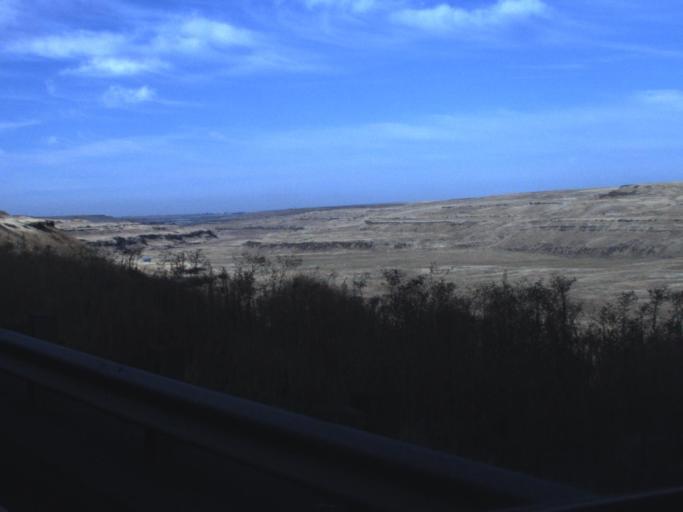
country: US
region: Washington
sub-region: Franklin County
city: Connell
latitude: 46.6324
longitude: -118.6368
